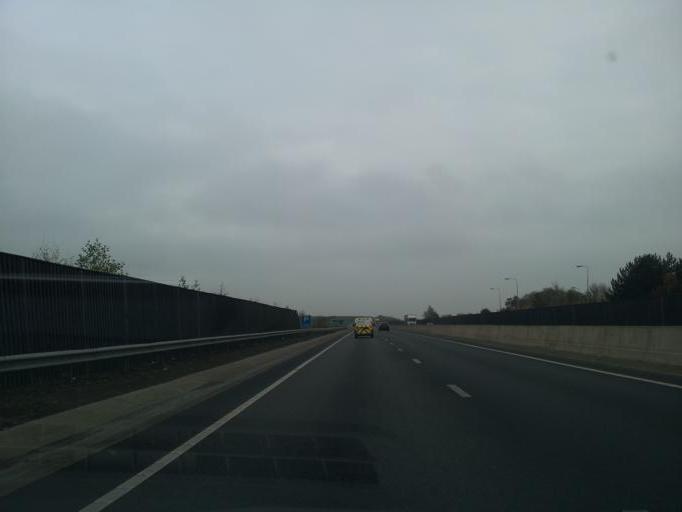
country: GB
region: England
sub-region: Central Bedfordshire
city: Marston Moretaine
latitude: 52.0725
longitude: -0.5419
